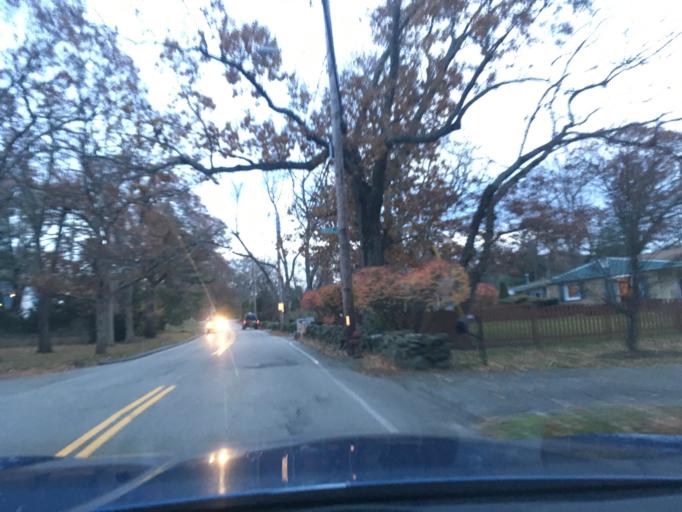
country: US
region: Rhode Island
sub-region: Kent County
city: East Greenwich
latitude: 41.6835
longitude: -71.4623
